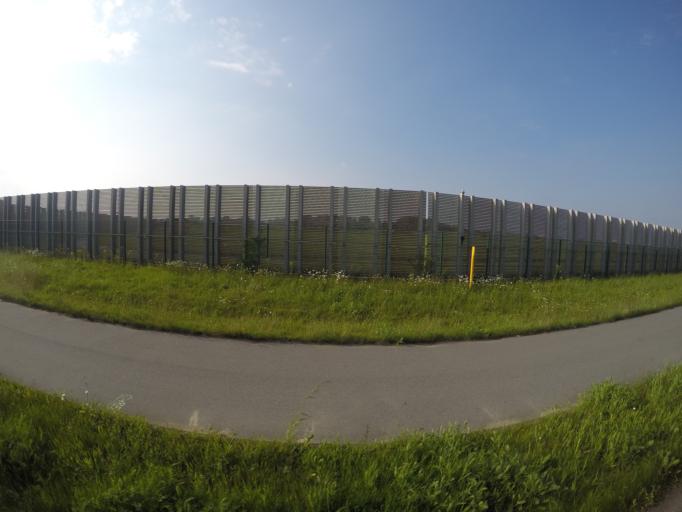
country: DE
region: Schleswig-Holstein
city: Halstenbek
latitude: 53.5659
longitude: 9.8269
